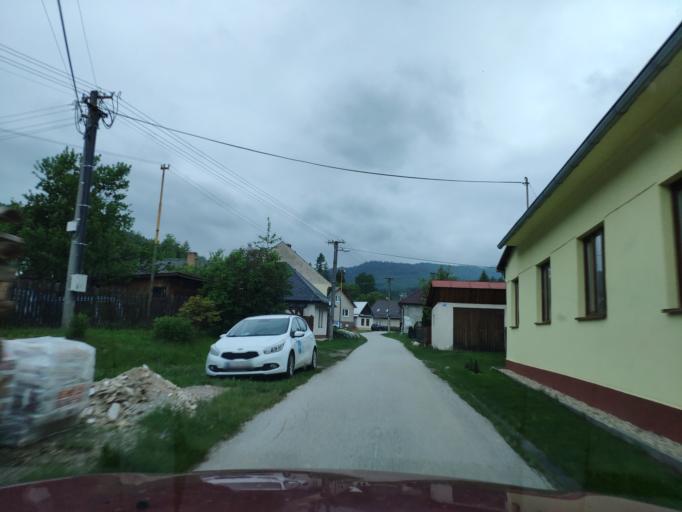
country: SK
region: Kosicky
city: Medzev
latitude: 48.7295
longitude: 20.7318
